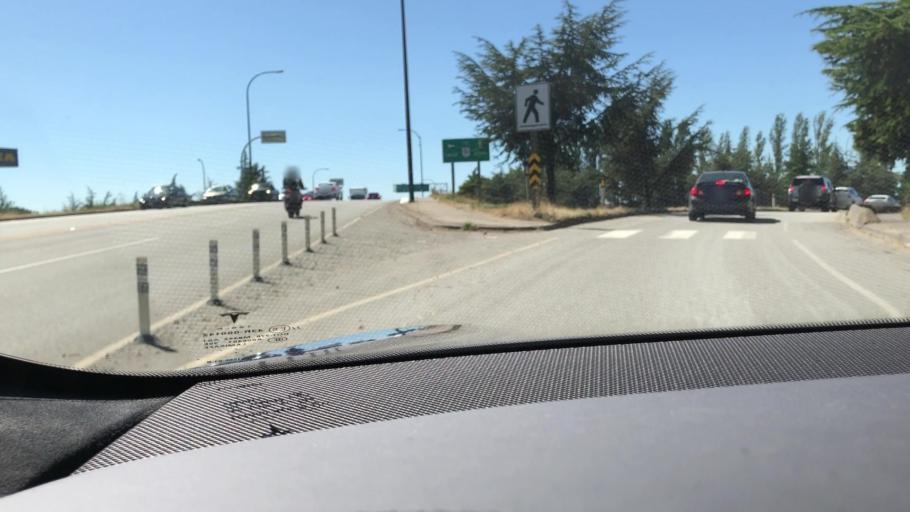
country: CA
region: British Columbia
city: Richmond
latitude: 49.1923
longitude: -123.0759
